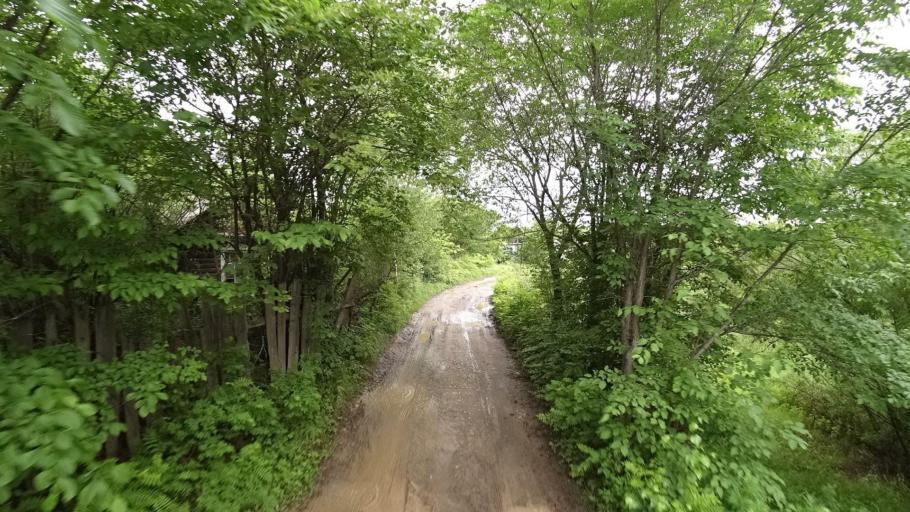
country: RU
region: Khabarovsk Krai
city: Amursk
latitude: 49.9055
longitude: 136.1323
